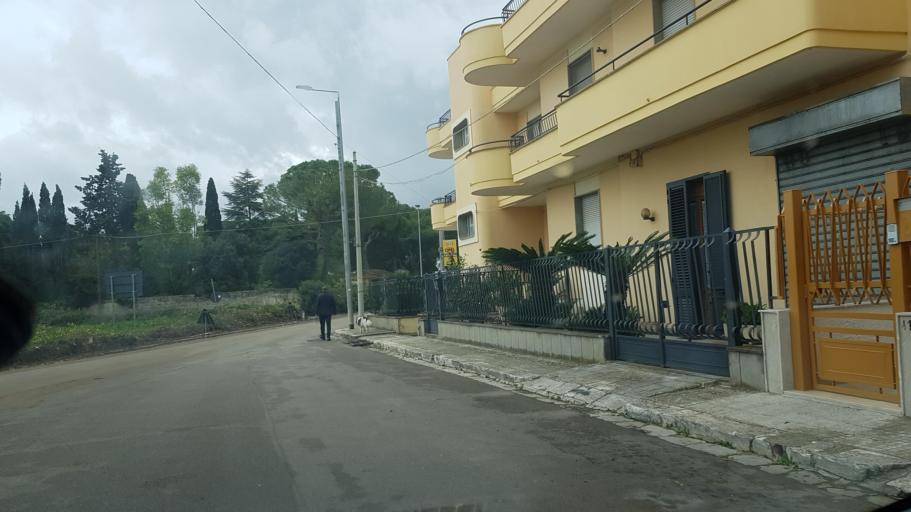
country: IT
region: Apulia
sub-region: Provincia di Lecce
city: Novoli
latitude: 40.3722
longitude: 18.0467
